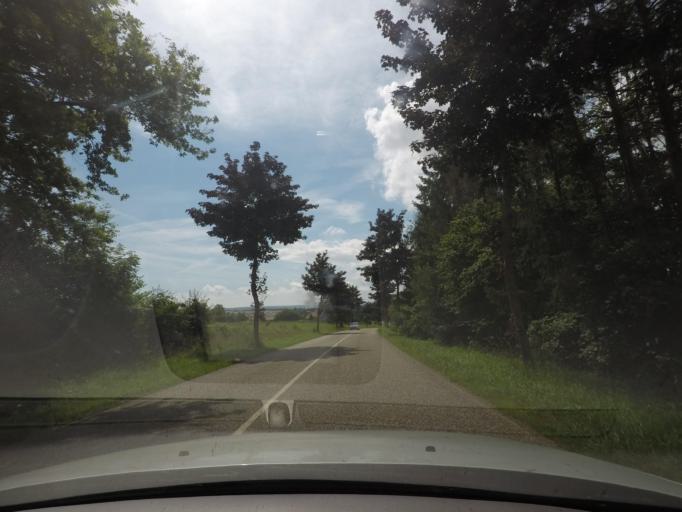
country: FR
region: Lorraine
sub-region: Departement de la Moselle
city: Phalsbourg
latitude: 48.8264
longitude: 7.2387
